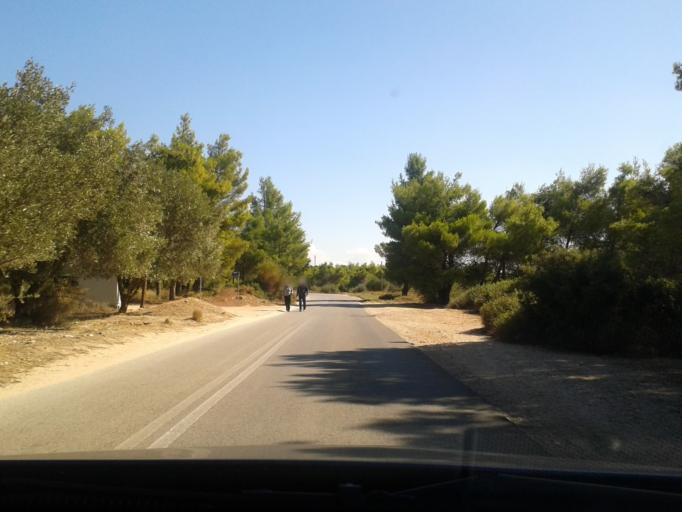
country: GR
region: Attica
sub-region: Nomarchia Anatolikis Attikis
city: Varybobi
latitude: 38.1322
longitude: 23.7752
